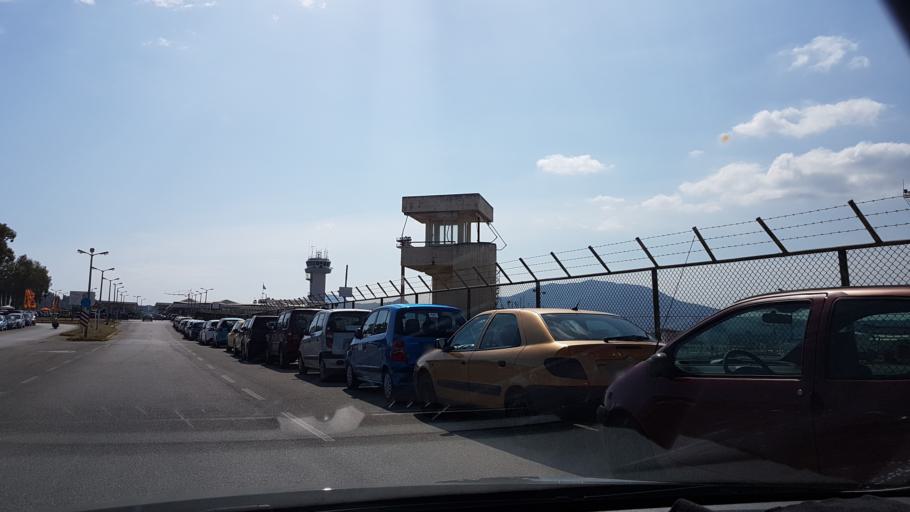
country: GR
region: Ionian Islands
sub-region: Nomos Kerkyras
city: Kerkyra
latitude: 39.6104
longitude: 19.9142
